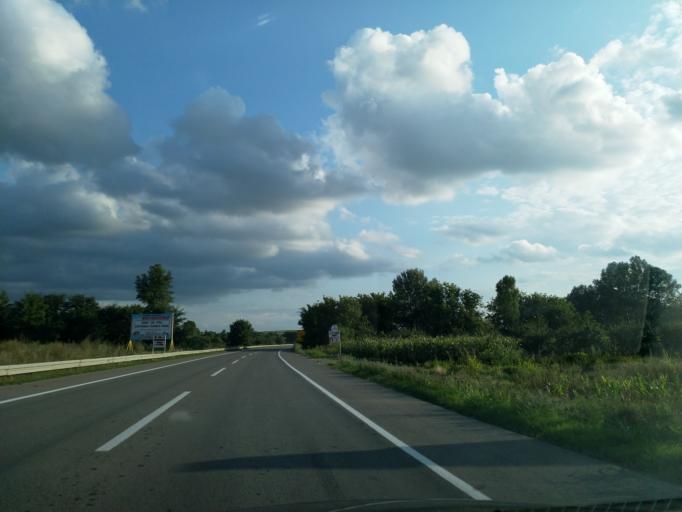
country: RS
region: Central Serbia
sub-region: Rasinski Okrug
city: Krusevac
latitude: 43.6251
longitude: 21.3744
